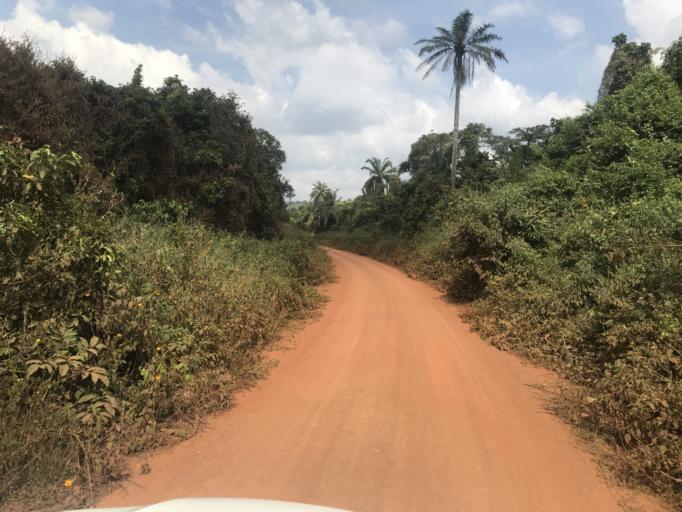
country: NG
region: Osun
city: Inisa
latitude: 7.8869
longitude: 4.3943
